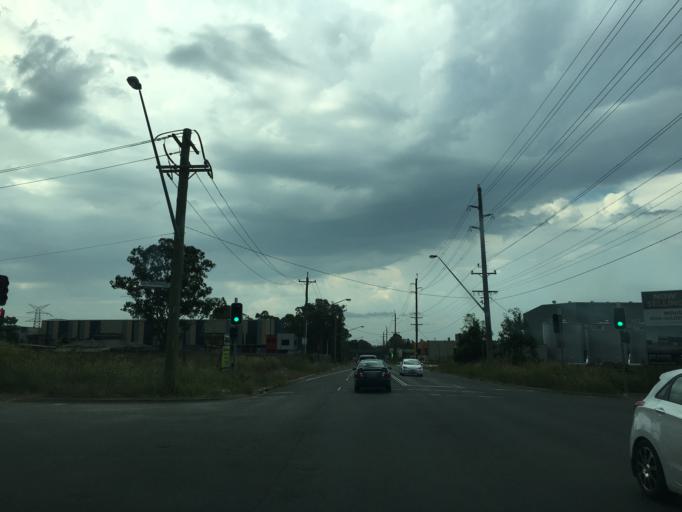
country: AU
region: New South Wales
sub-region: Liverpool
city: Miller
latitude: -33.9385
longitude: 150.8680
